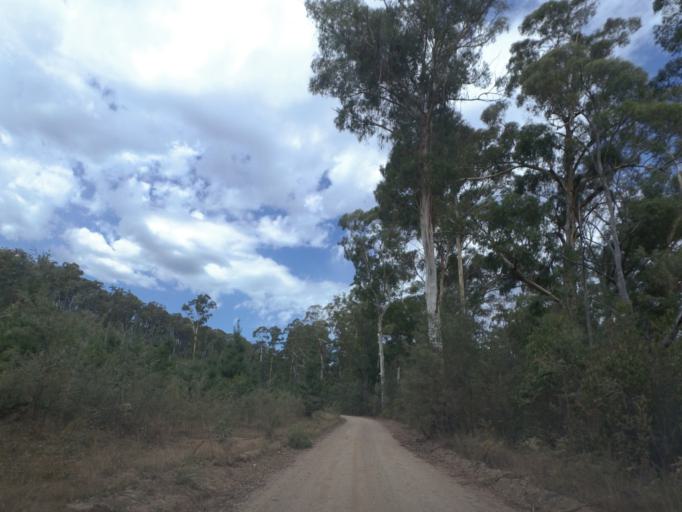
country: AU
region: Victoria
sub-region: Murrindindi
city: Alexandra
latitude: -37.3770
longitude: 145.7601
